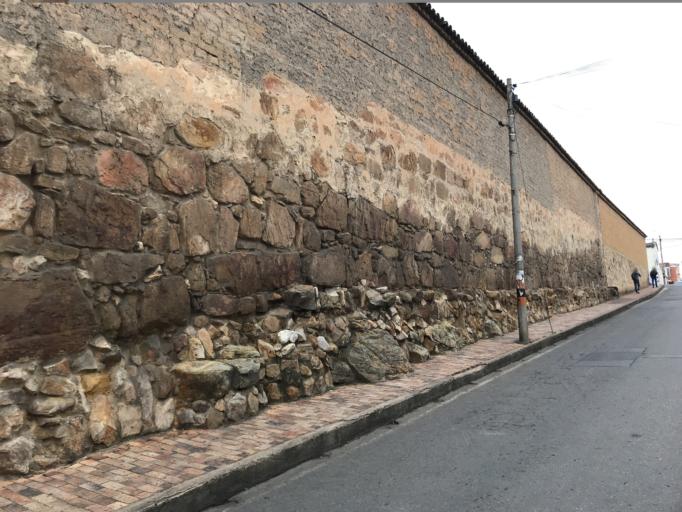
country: CO
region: Boyaca
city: Tunja
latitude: 5.5352
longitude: -73.3580
